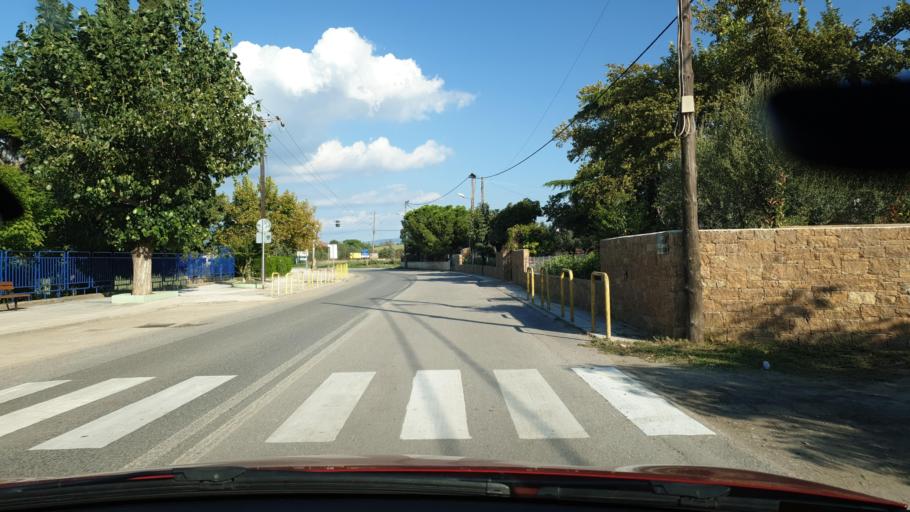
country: GR
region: Central Macedonia
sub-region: Nomos Thessalonikis
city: Agia Paraskevi
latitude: 40.4833
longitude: 23.0513
